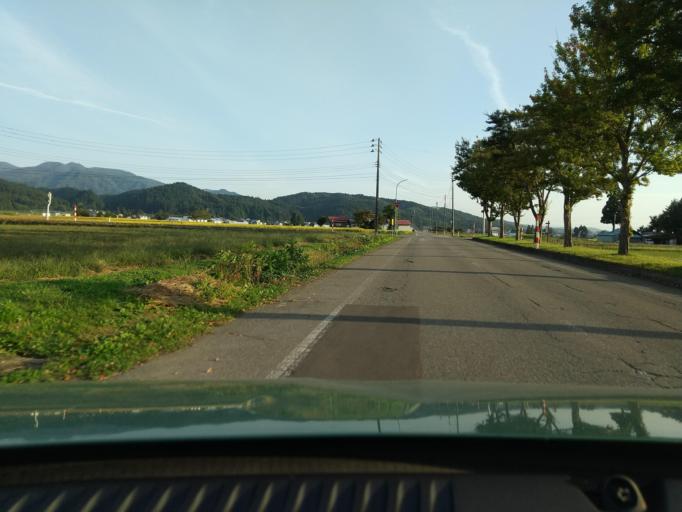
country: JP
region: Akita
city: Omagari
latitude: 39.4606
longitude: 140.5840
